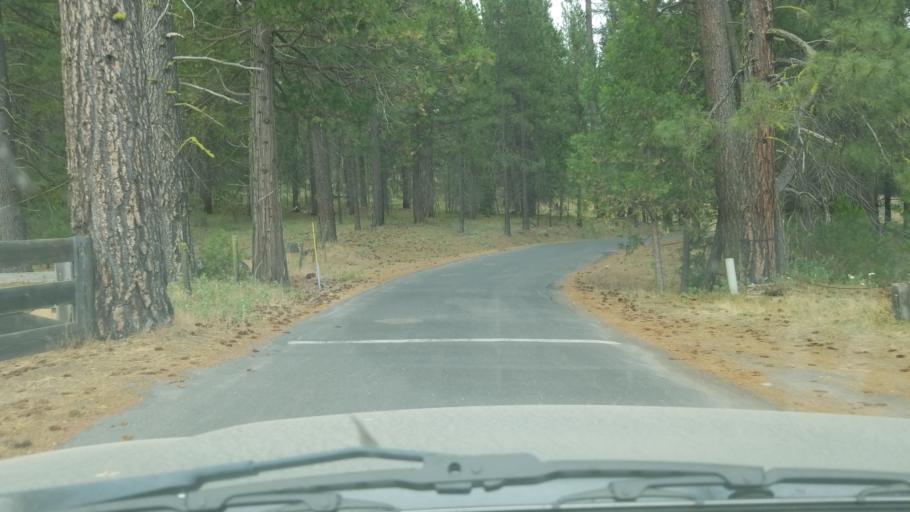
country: US
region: California
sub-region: Mariposa County
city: Yosemite Valley
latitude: 37.8492
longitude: -119.8587
